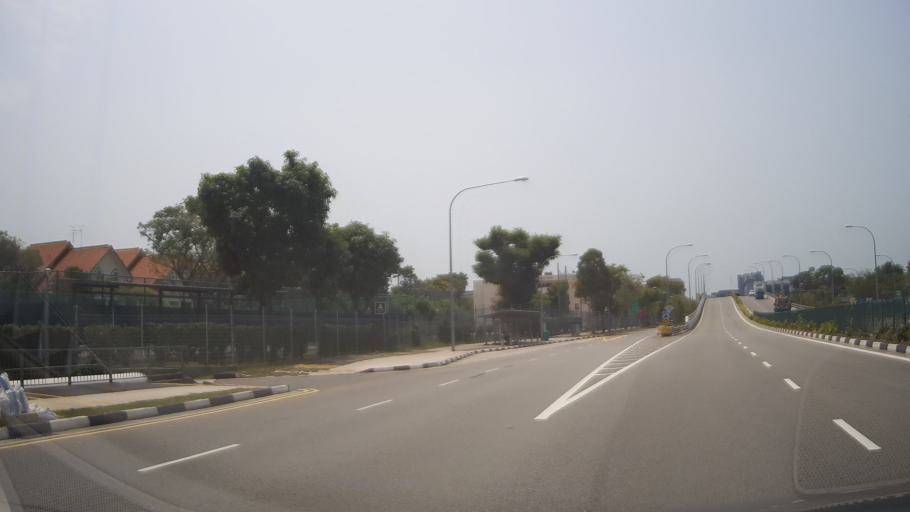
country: SG
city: Singapore
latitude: 1.3131
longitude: 103.7545
